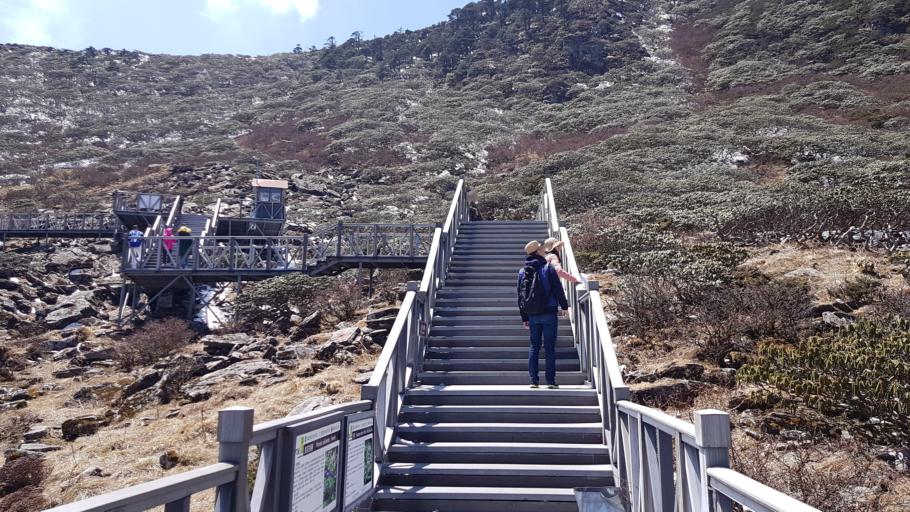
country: CN
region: Yunnan
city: Shangjie
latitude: 25.6607
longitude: 100.0995
